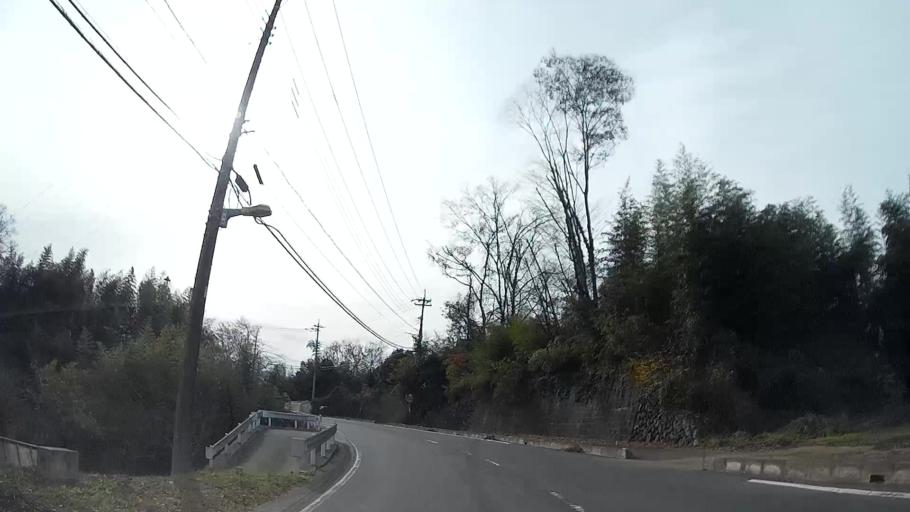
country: JP
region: Saitama
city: Chichibu
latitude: 35.9924
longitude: 139.0325
